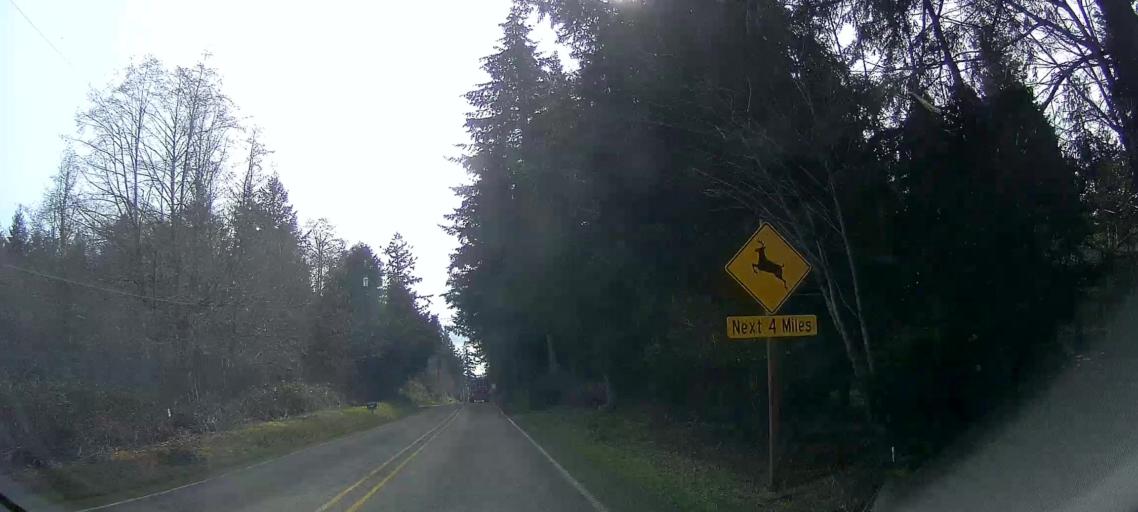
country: US
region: Washington
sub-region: Island County
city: Langley
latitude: 48.0713
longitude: -122.3877
